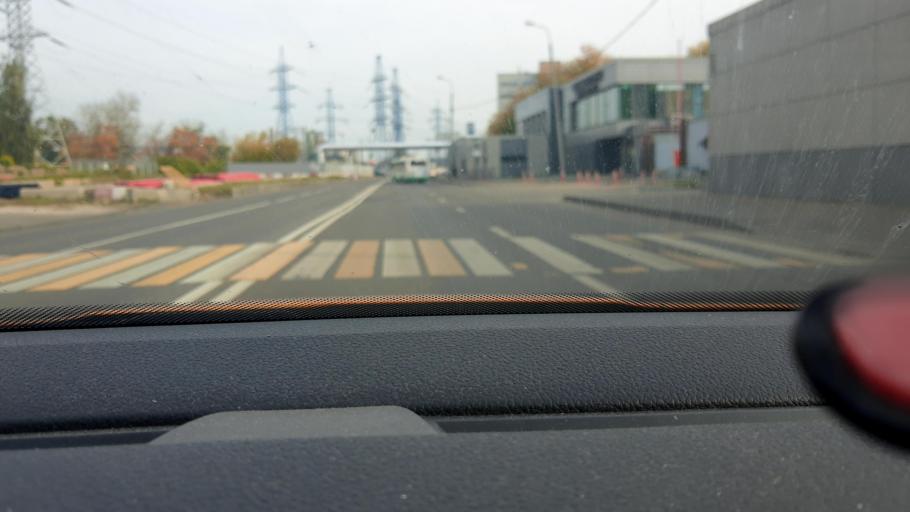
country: RU
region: Moscow
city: Leonovo
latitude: 55.8477
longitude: 37.6563
